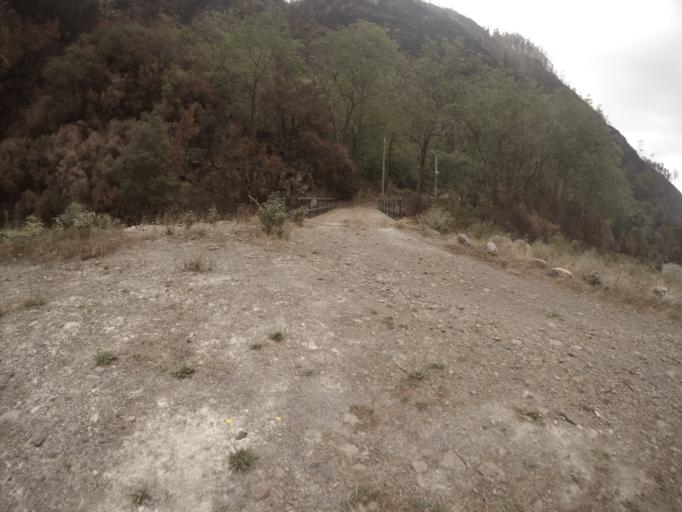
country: PT
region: Madeira
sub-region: Funchal
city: Nossa Senhora do Monte
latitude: 32.6945
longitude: -16.9169
